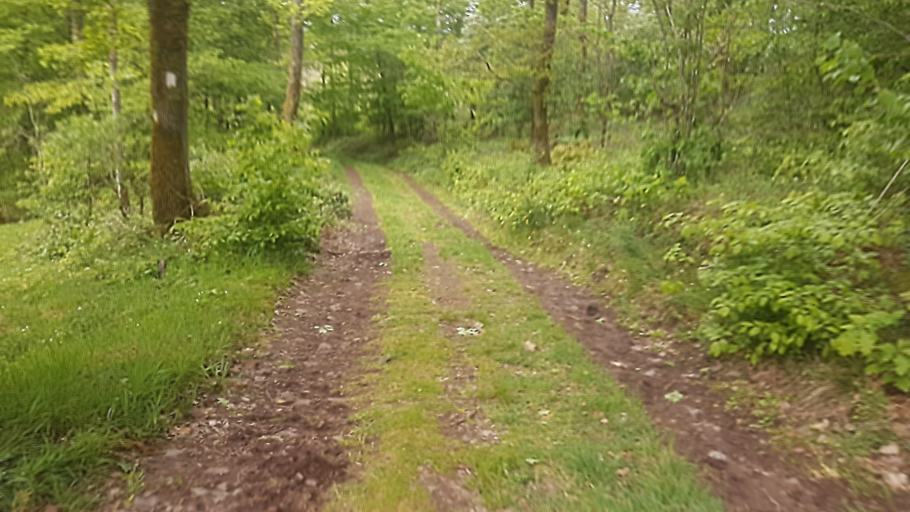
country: FR
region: Champagne-Ardenne
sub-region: Departement des Ardennes
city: Haybes
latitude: 50.0641
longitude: 4.6223
